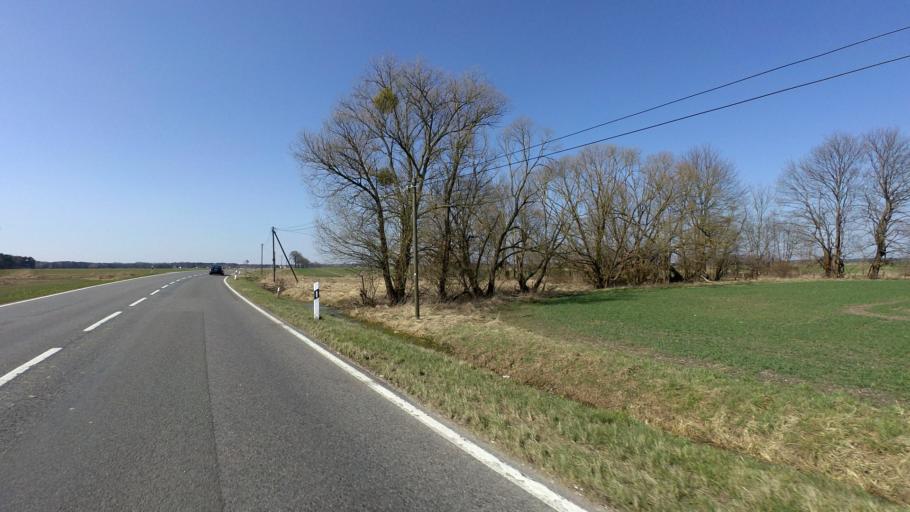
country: DE
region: Brandenburg
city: Ruthnick
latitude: 52.8996
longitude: 13.0019
